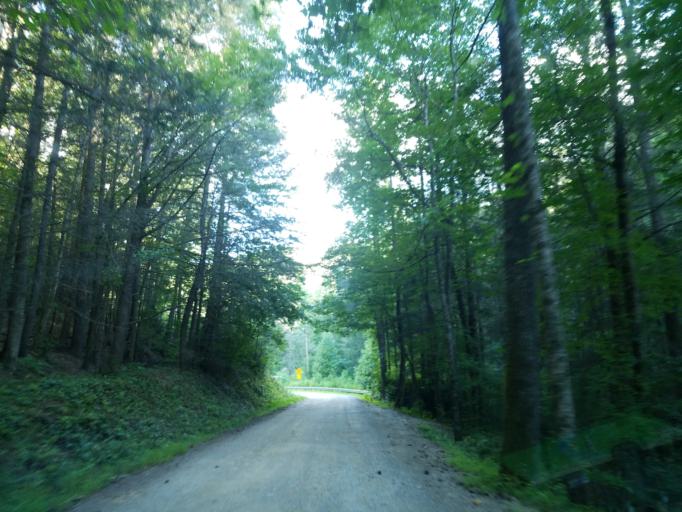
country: US
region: Georgia
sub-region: Union County
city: Blairsville
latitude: 34.7598
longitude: -84.0676
